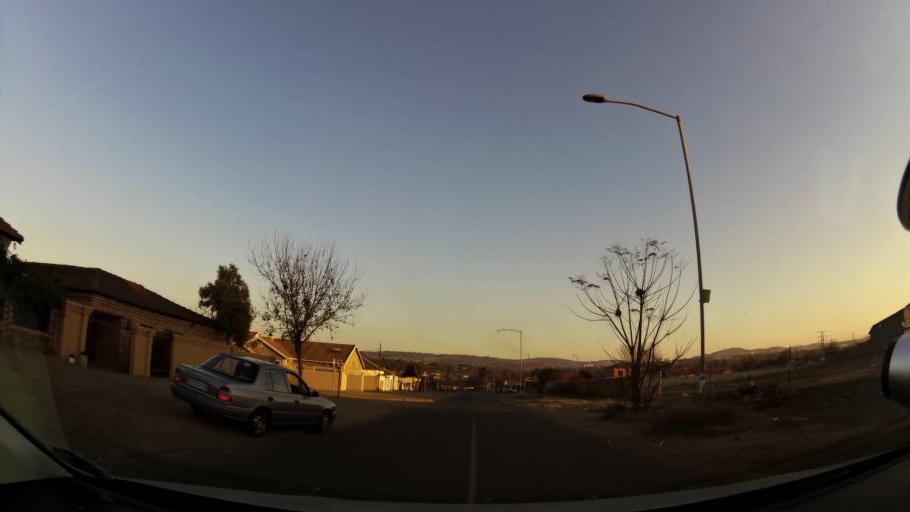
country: ZA
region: Gauteng
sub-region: City of Tshwane Metropolitan Municipality
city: Pretoria
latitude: -25.7415
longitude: 28.1376
